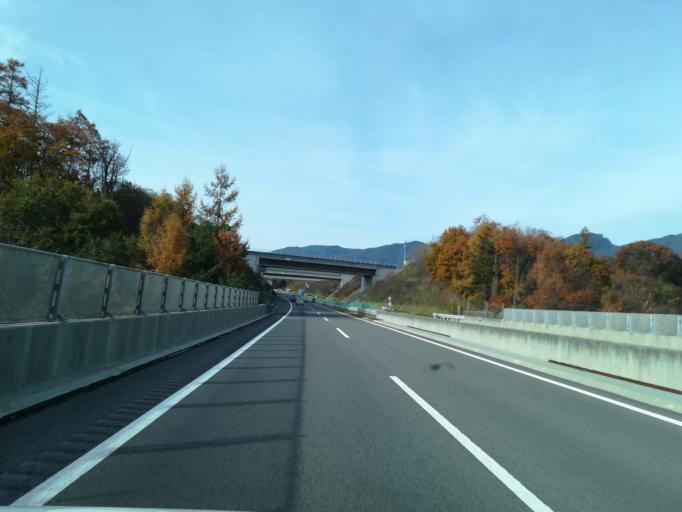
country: JP
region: Nagano
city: Komoro
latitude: 36.3168
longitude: 138.4784
